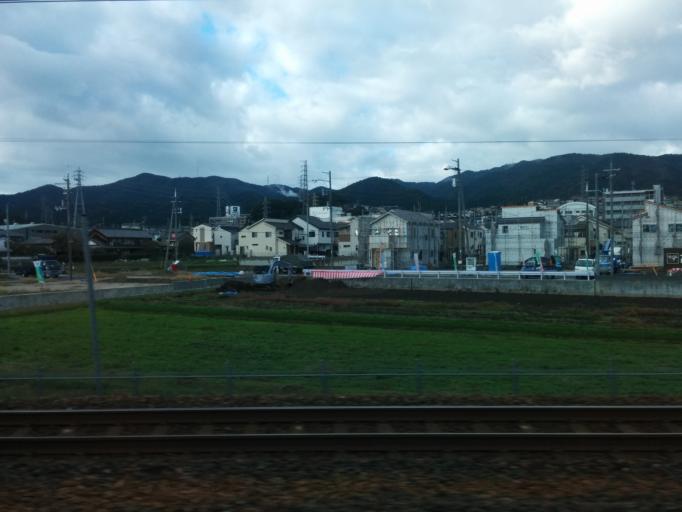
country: JP
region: Shiga Prefecture
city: Otsu-shi
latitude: 34.9860
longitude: 135.8910
